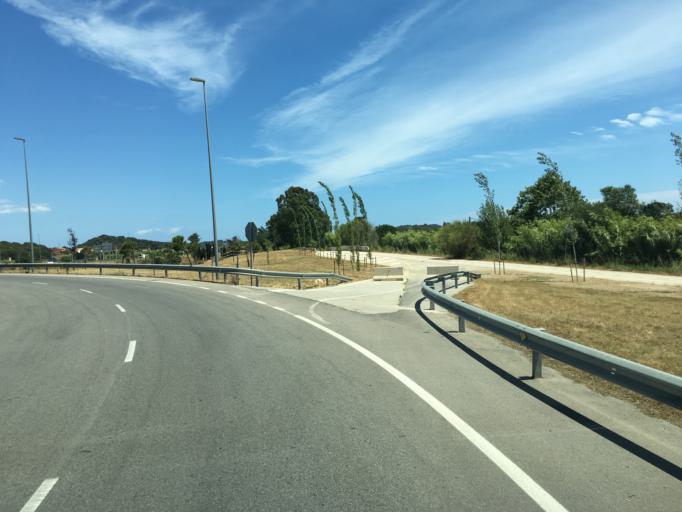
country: ES
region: Catalonia
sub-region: Provincia de Girona
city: Palamos
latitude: 41.8564
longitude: 3.1207
